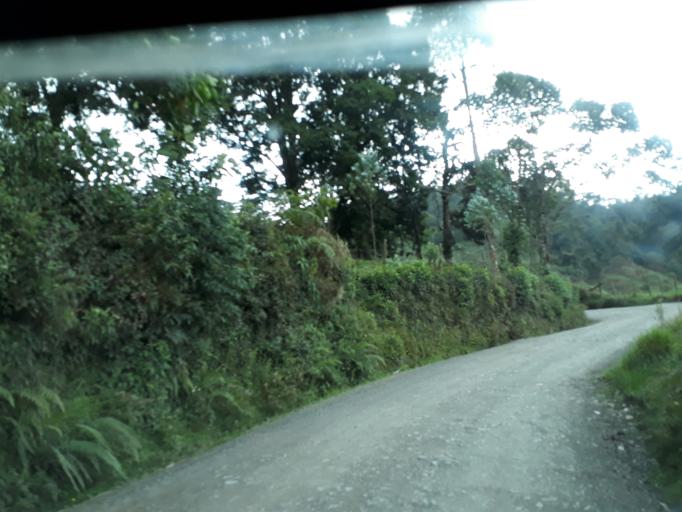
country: CO
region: Cundinamarca
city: Pacho
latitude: 5.2410
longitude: -74.1835
